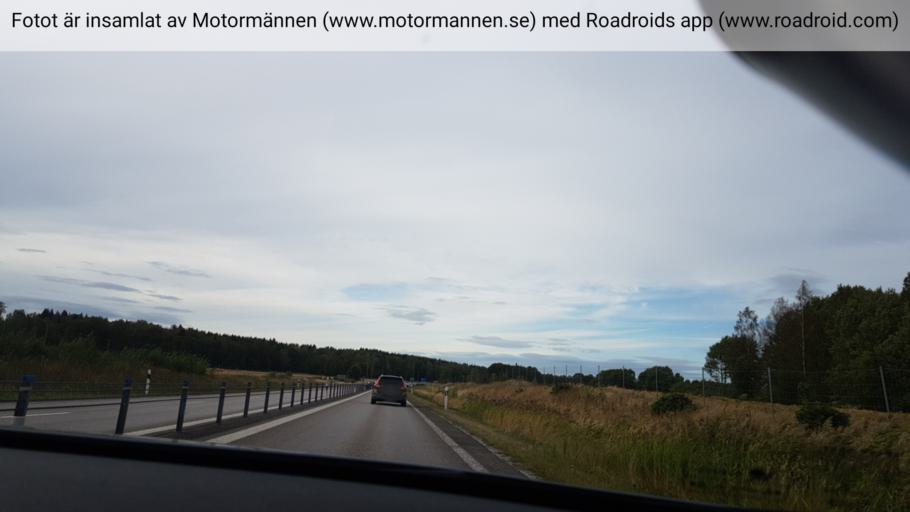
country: SE
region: Vaestra Goetaland
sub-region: Mariestads Kommun
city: Mariestad
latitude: 58.5881
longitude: 13.7999
